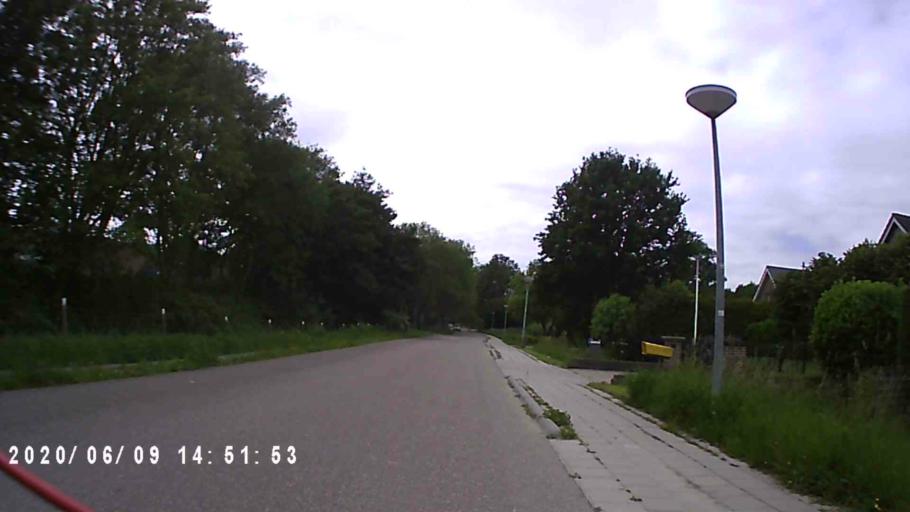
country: NL
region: Groningen
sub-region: Gemeente Winsum
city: Winsum
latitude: 53.3313
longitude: 6.5282
